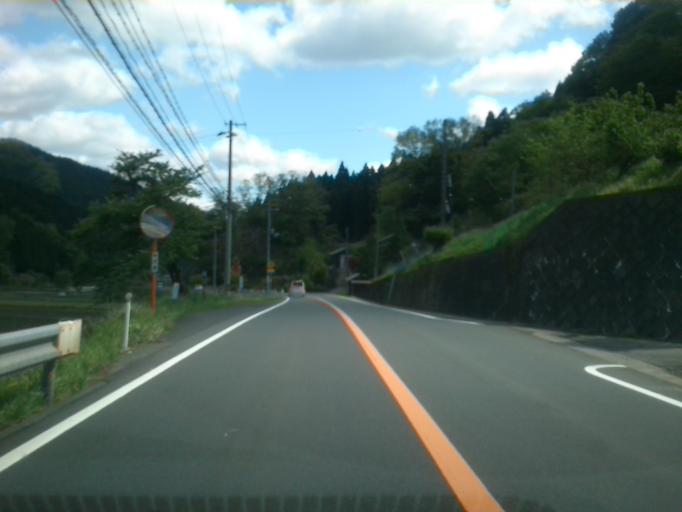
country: JP
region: Kyoto
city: Fukuchiyama
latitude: 35.3712
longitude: 135.0464
